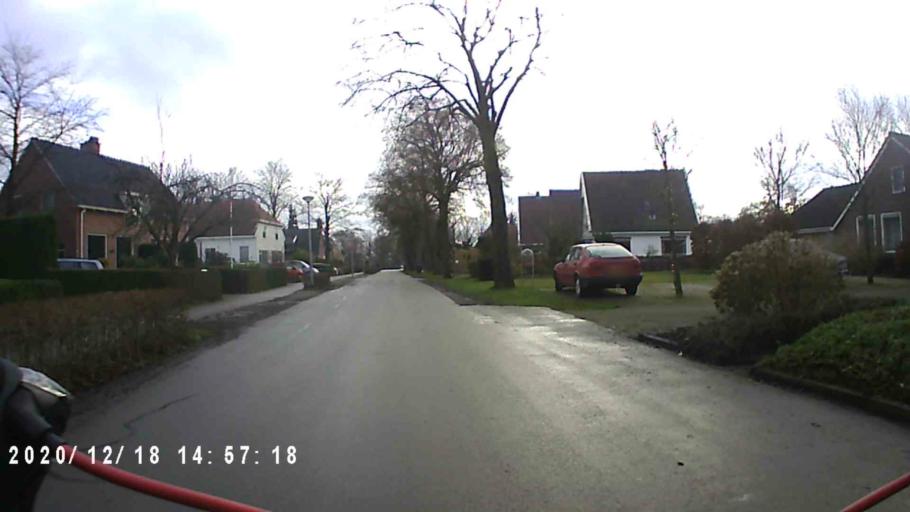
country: NL
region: Groningen
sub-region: Gemeente Hoogezand-Sappemeer
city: Hoogezand
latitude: 53.1816
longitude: 6.6883
